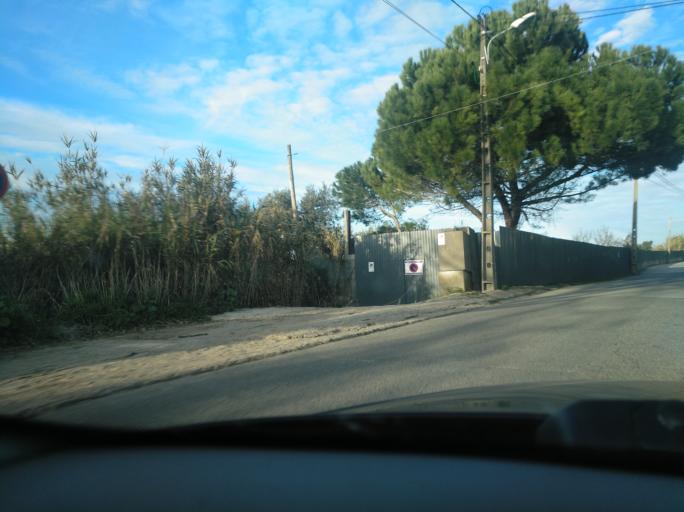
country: PT
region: Lisbon
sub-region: Loures
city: Unhos
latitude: 38.8325
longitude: -9.1315
